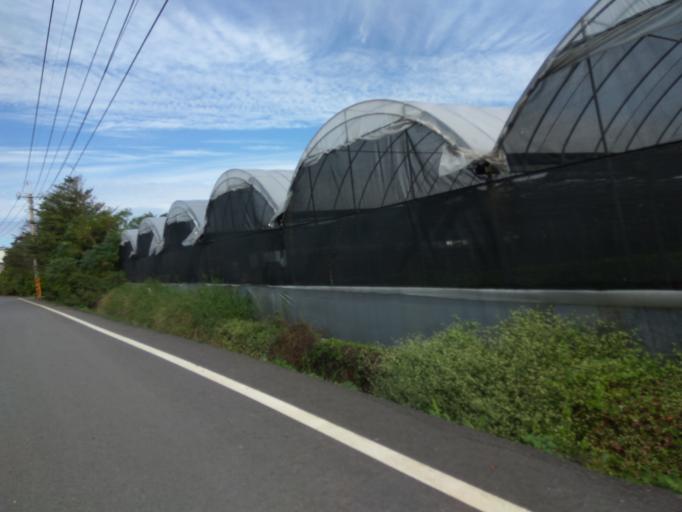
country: TW
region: Taiwan
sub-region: Hsinchu
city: Zhubei
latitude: 24.9964
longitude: 121.0916
